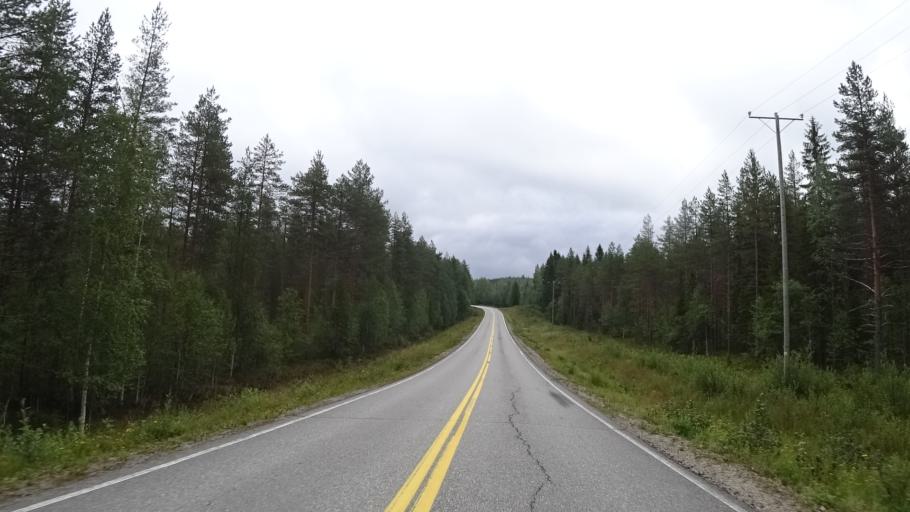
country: FI
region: North Karelia
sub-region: Joensuu
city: Ilomantsi
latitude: 63.2598
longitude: 30.6626
